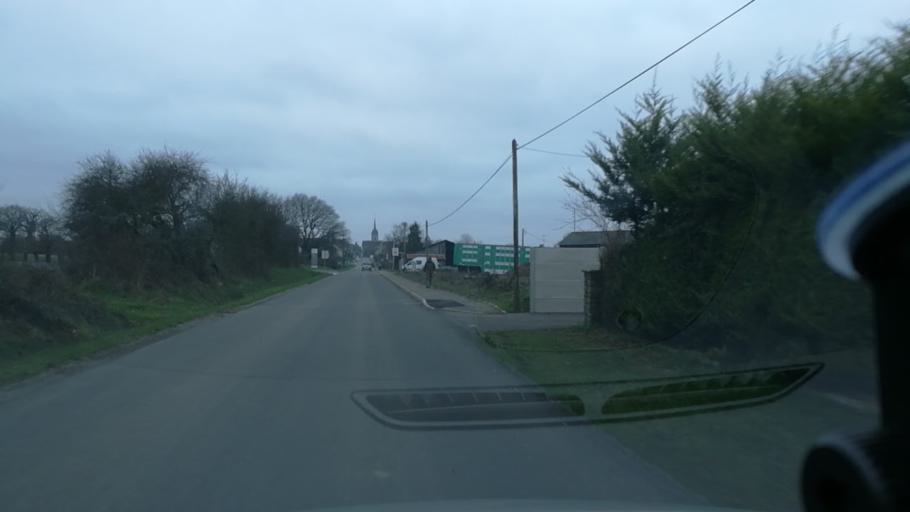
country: FR
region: Brittany
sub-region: Departement d'Ille-et-Vilaine
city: Tresboeuf
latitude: 47.8826
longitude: -1.5384
